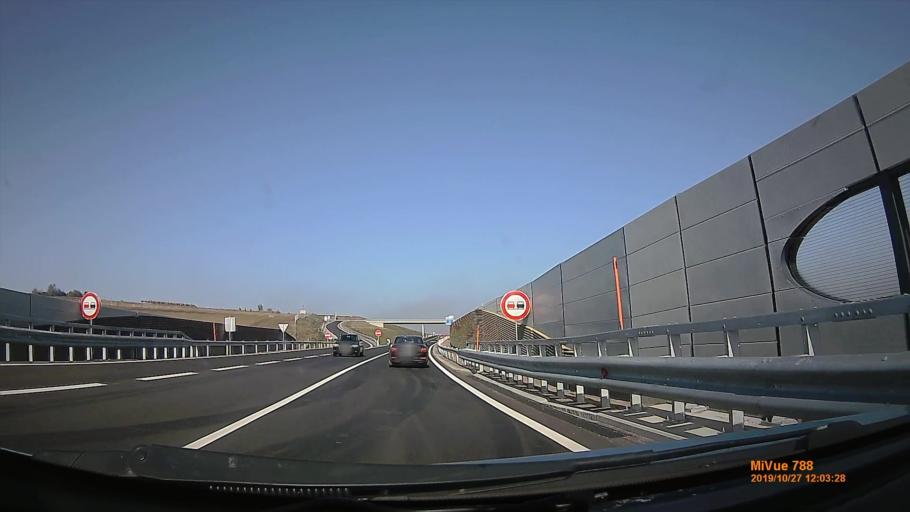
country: AT
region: Lower Austria
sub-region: Politischer Bezirk Mistelbach
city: Drasenhofen
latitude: 48.7428
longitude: 16.6374
